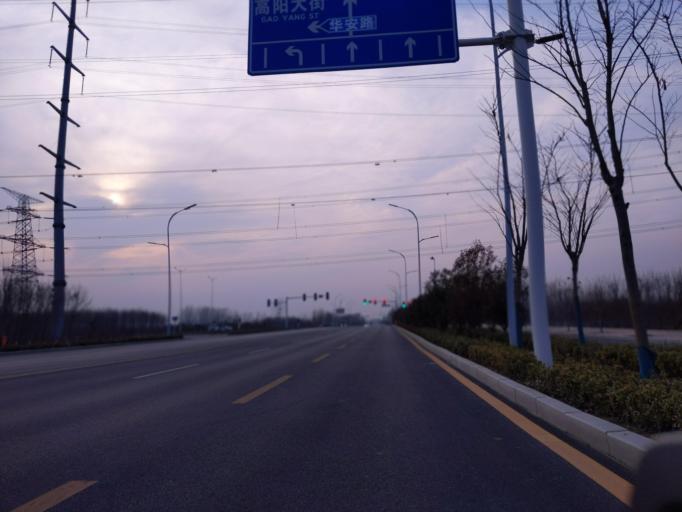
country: CN
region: Henan Sheng
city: Puyang
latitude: 35.8190
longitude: 114.9978
